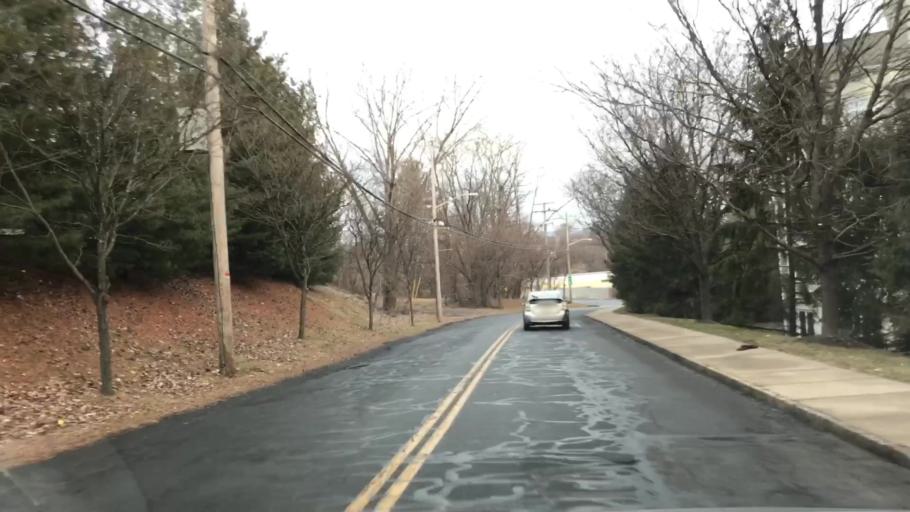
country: US
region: New York
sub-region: Rockland County
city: Haverstraw
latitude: 41.1902
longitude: -73.9600
